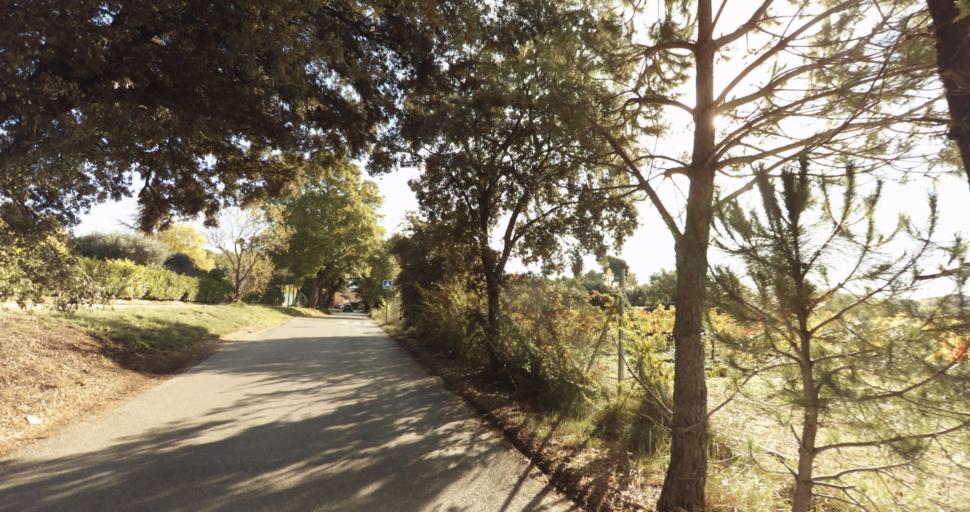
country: FR
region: Provence-Alpes-Cote d'Azur
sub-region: Departement des Bouches-du-Rhone
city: Venelles
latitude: 43.5897
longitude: 5.4705
